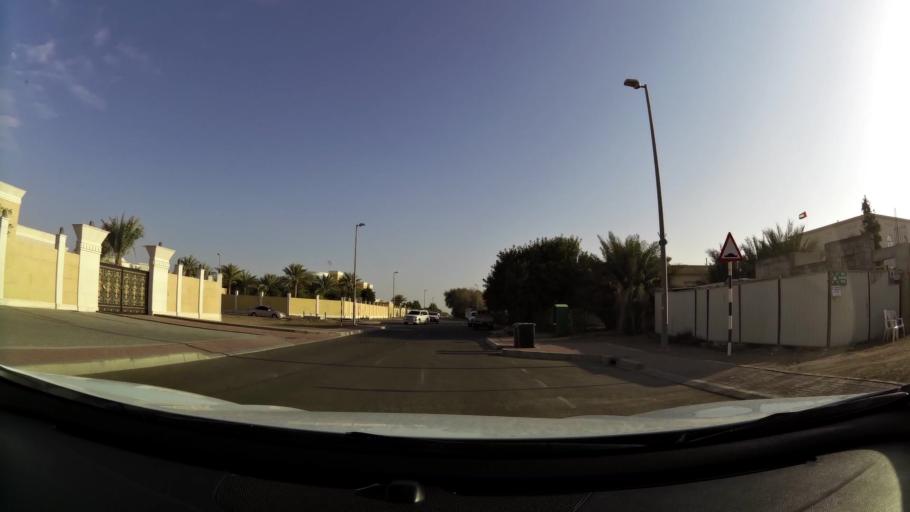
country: AE
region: Abu Dhabi
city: Al Ain
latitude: 24.0860
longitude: 55.8476
